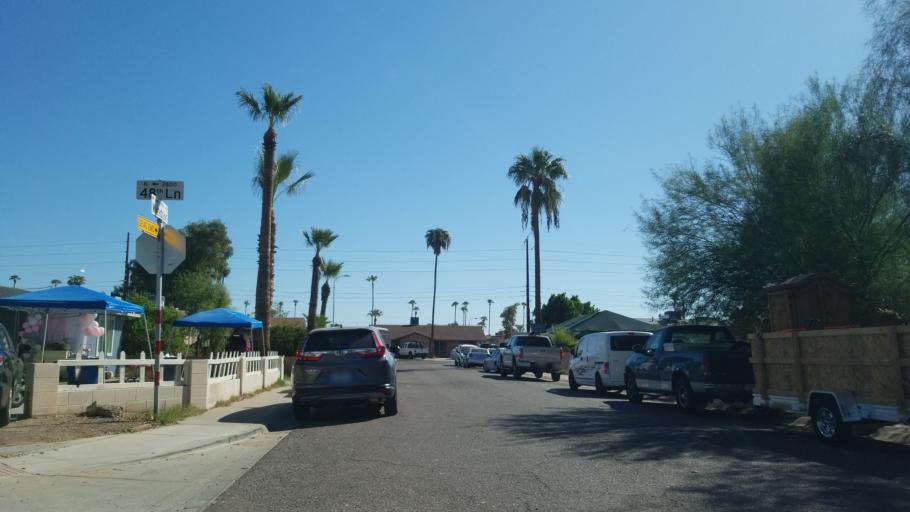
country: US
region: Arizona
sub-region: Maricopa County
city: Glendale
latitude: 33.4793
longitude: -112.1616
